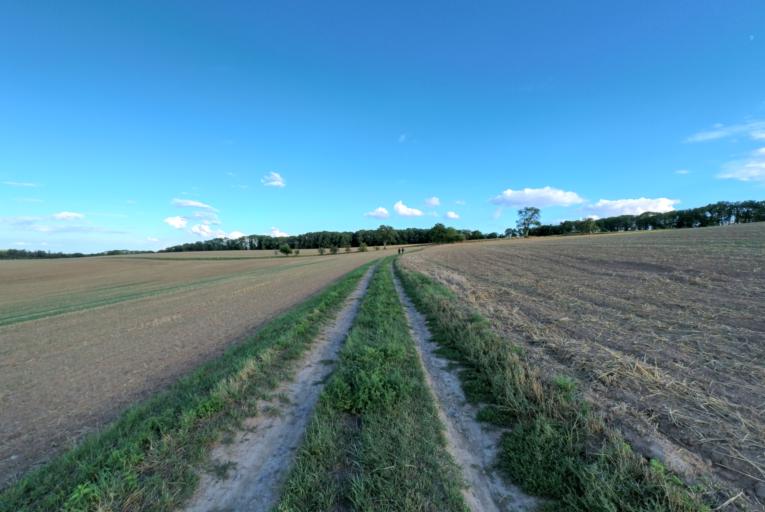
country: DE
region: Baden-Wuerttemberg
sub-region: Karlsruhe Region
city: Mosbach
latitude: 49.3339
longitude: 9.1698
